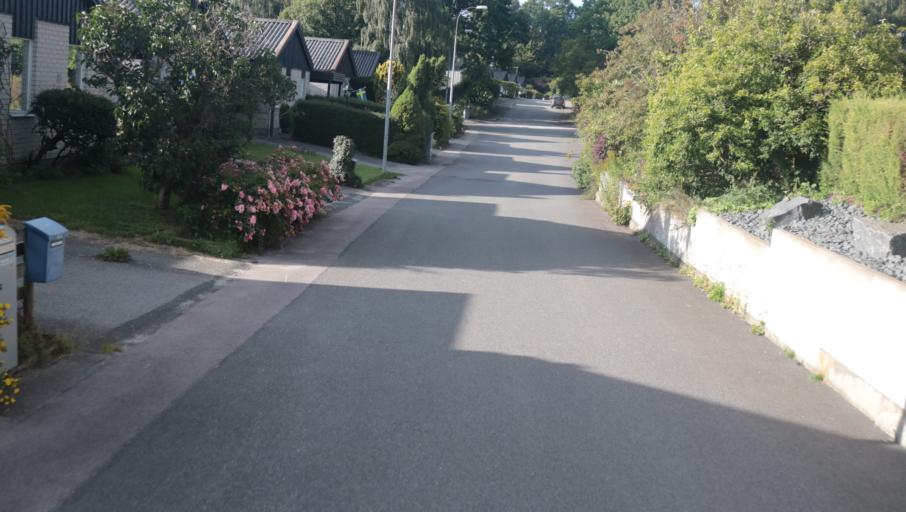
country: SE
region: Blekinge
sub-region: Karlshamns Kommun
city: Karlshamn
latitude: 56.1622
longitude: 14.8905
